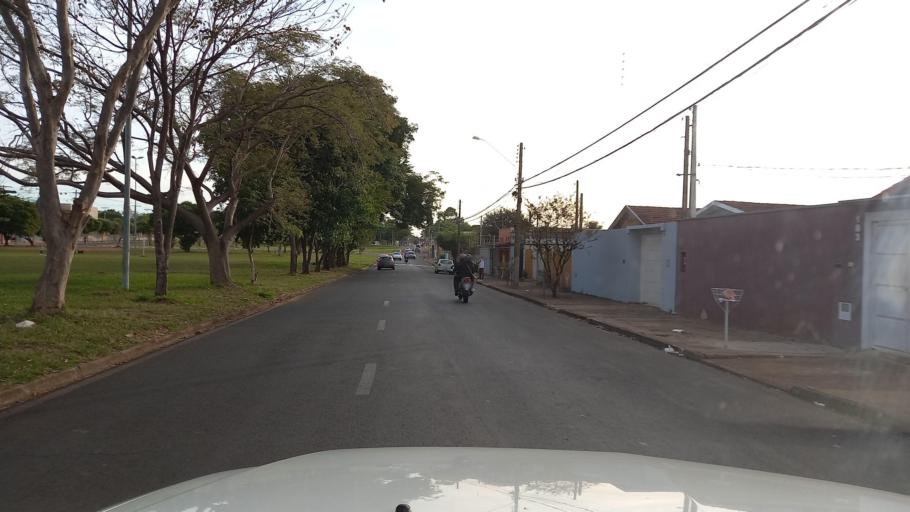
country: BR
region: Sao Paulo
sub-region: Moji-Guacu
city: Mogi-Gaucu
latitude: -22.3443
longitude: -46.9314
